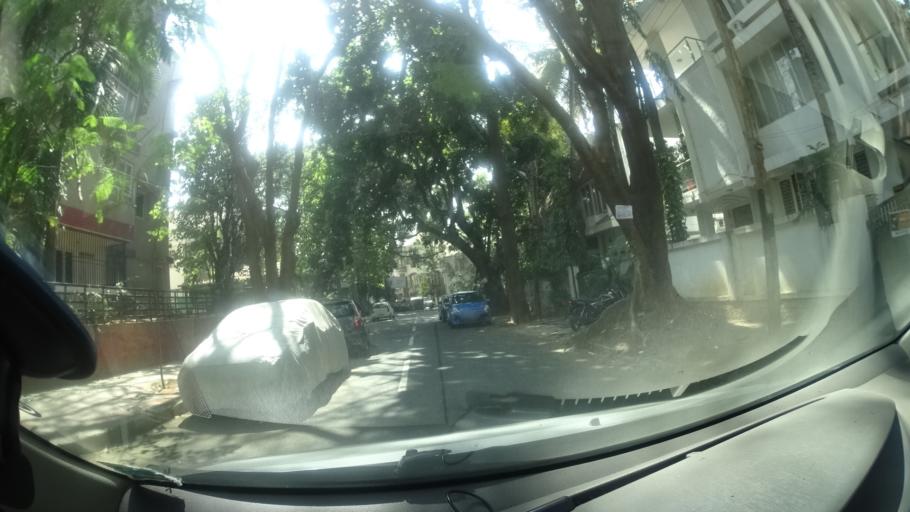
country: IN
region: Karnataka
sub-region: Bangalore Urban
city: Bangalore
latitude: 13.0099
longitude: 77.5765
